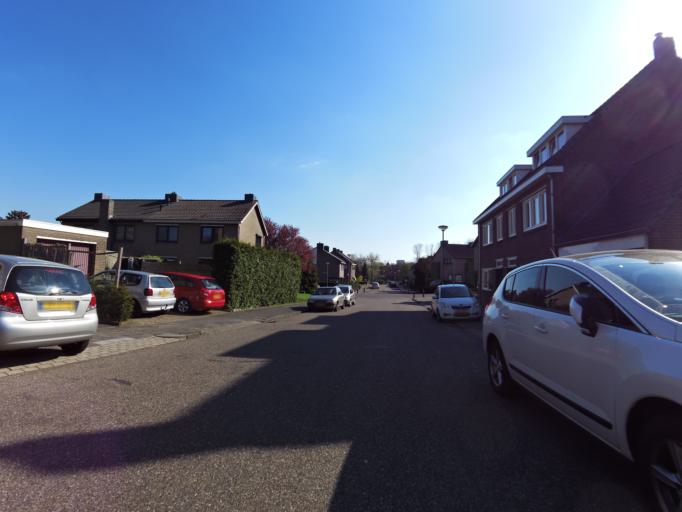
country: NL
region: Limburg
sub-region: Gemeente Heerlen
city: Heerlen
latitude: 50.8983
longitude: 6.0214
